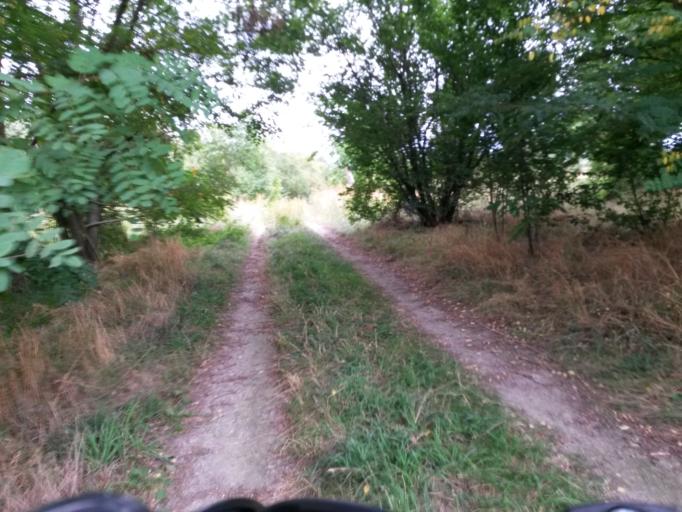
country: DE
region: Brandenburg
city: Angermunde
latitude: 53.0355
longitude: 13.9664
